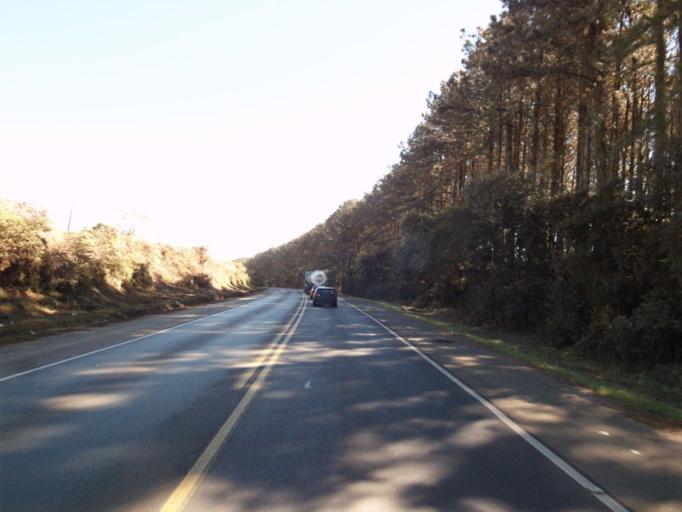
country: BR
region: Santa Catarina
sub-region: Xanxere
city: Xanxere
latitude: -26.8726
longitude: -52.2909
